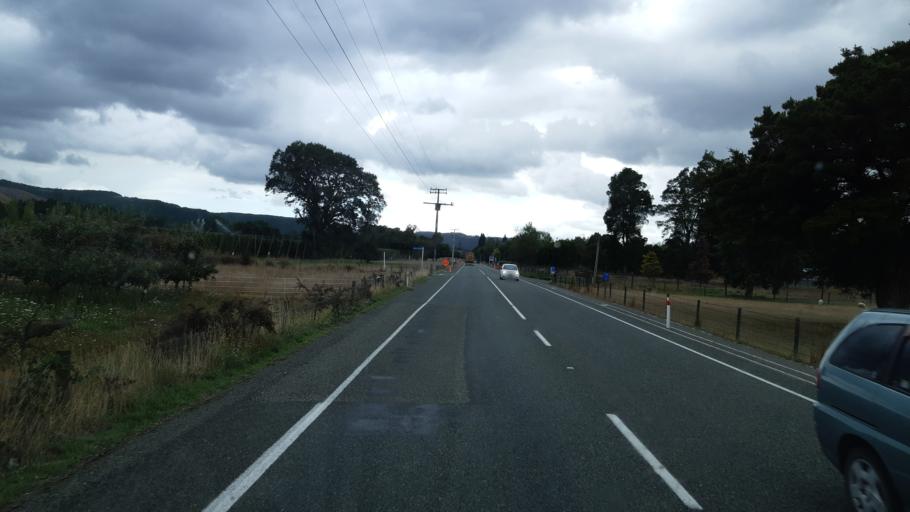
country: NZ
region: Tasman
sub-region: Tasman District
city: Wakefield
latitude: -41.4202
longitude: 173.0063
